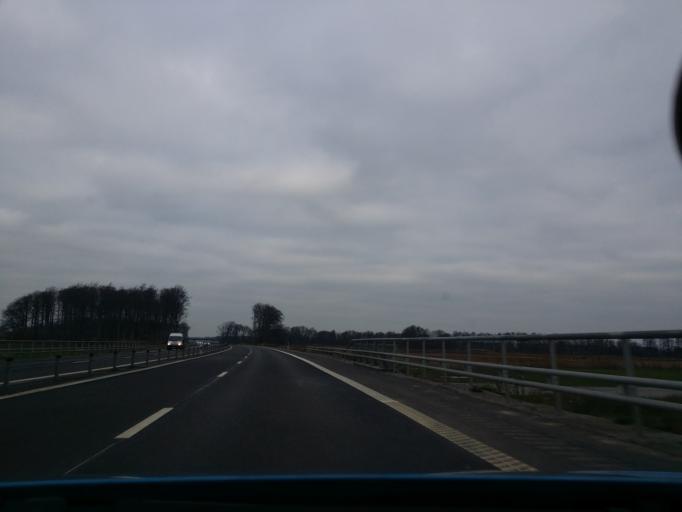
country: SE
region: Blekinge
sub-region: Solvesborgs Kommun
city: Soelvesborg
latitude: 56.1095
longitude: 14.6592
